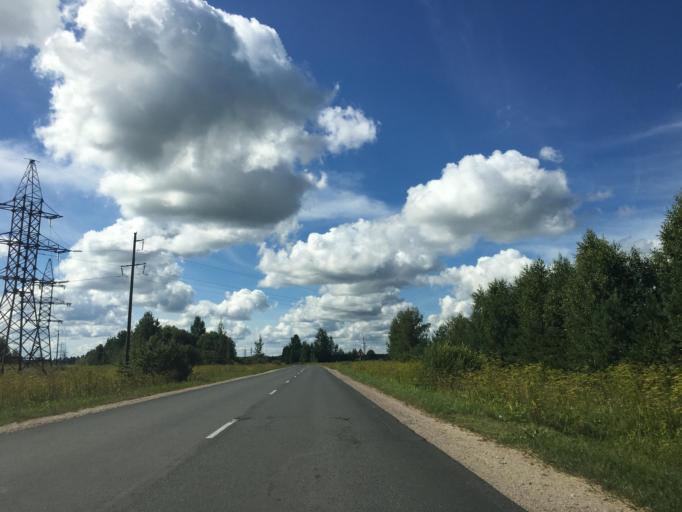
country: RU
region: Pskov
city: Pskov
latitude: 57.7759
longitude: 28.1646
